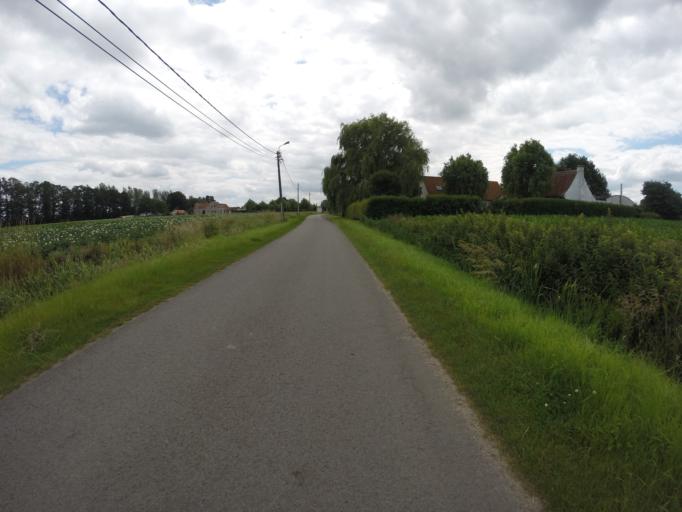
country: BE
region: Flanders
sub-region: Provincie Oost-Vlaanderen
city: Aalter
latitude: 51.1200
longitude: 3.4440
